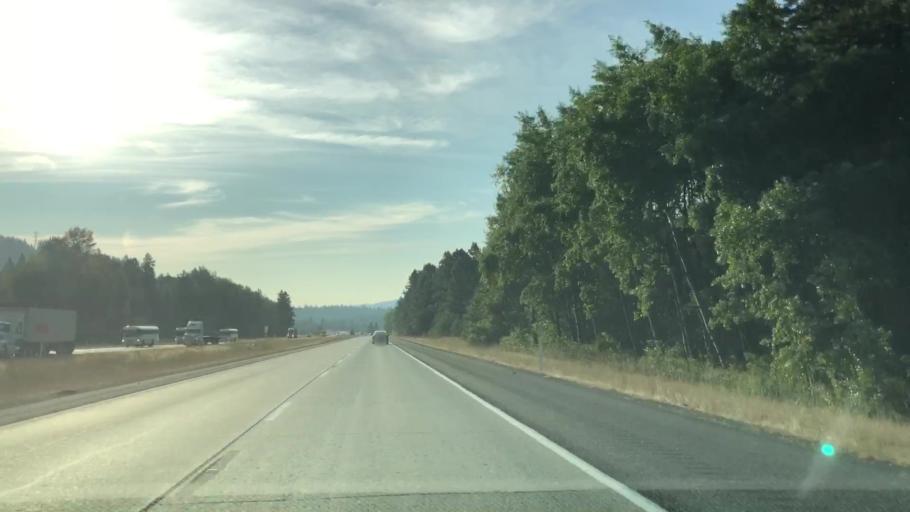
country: US
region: Washington
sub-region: Kittitas County
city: Cle Elum
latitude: 47.2008
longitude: -121.0670
